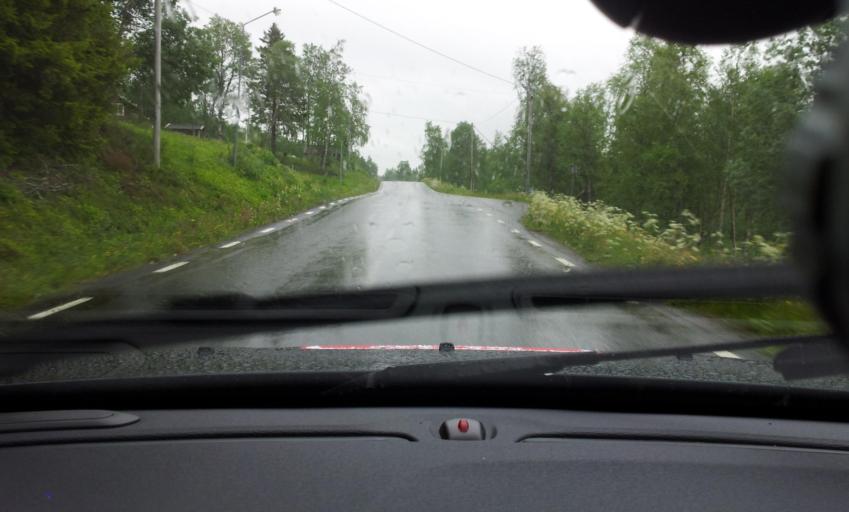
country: SE
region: Jaemtland
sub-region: Are Kommun
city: Are
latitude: 63.3149
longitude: 13.0717
